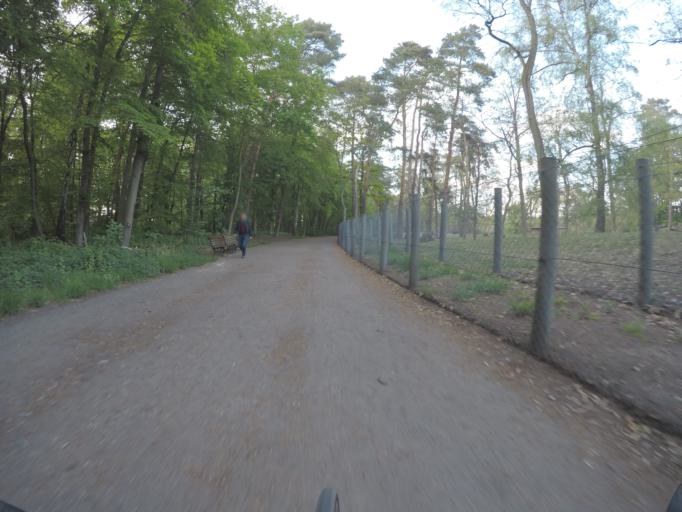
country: DE
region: Berlin
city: Reinickendorf
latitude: 52.5510
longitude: 13.3246
